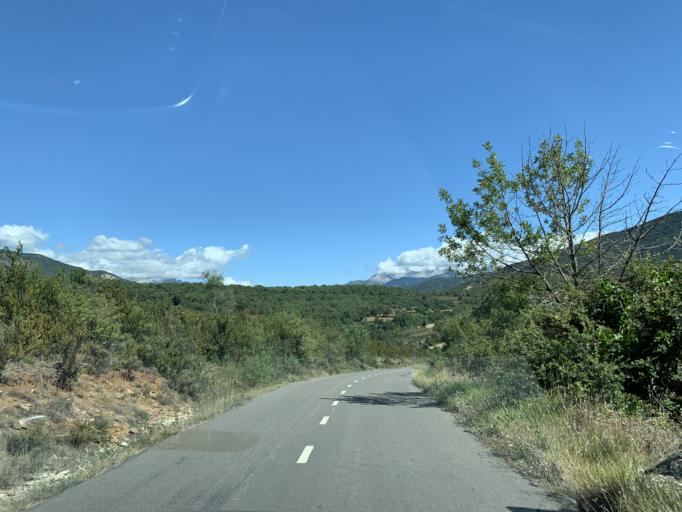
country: ES
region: Aragon
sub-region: Provincia de Huesca
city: Sabinanigo
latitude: 42.5326
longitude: -0.3234
